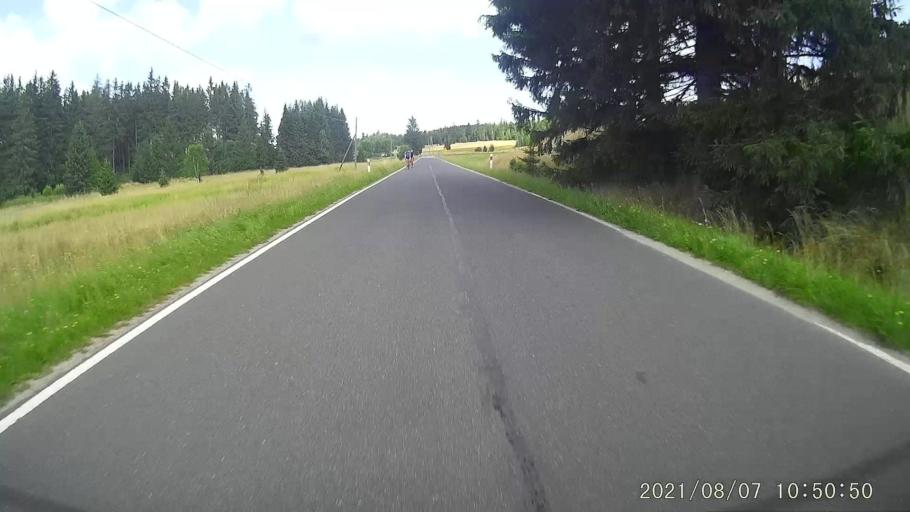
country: PL
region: Lower Silesian Voivodeship
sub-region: Powiat klodzki
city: Polanica-Zdroj
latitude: 50.2941
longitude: 16.4663
